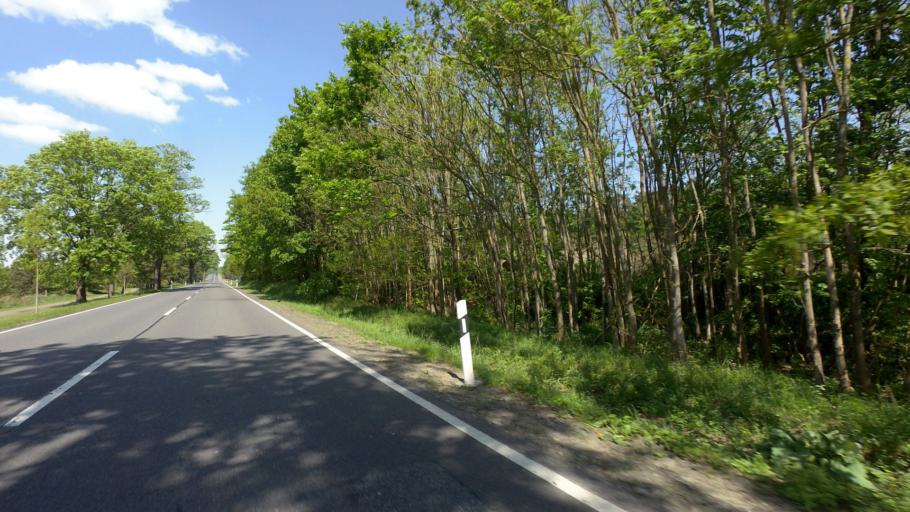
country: DE
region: Mecklenburg-Vorpommern
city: Neustrelitz
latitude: 53.4040
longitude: 13.0428
